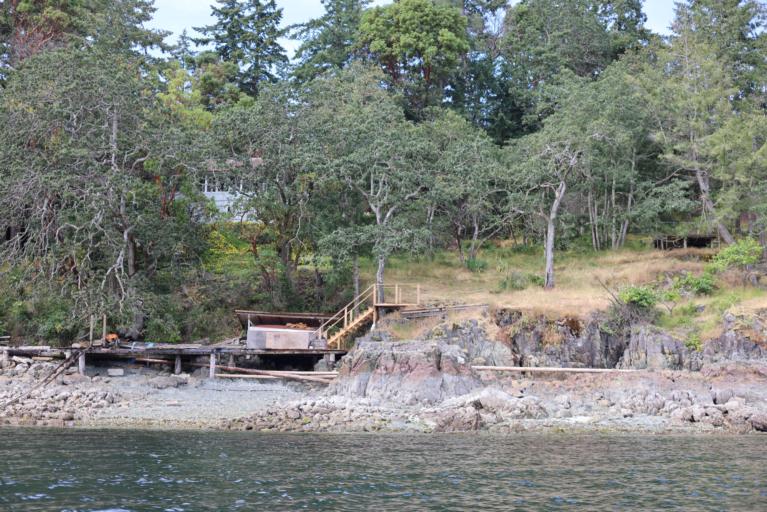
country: CA
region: British Columbia
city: Nanaimo
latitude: 49.2108
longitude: -123.9460
